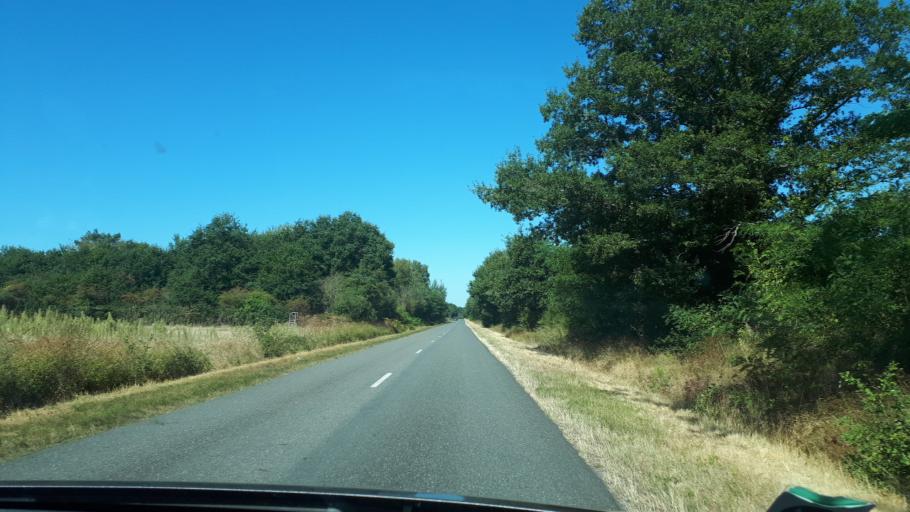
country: FR
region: Centre
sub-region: Departement du Loiret
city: Cerdon
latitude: 47.6385
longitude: 2.4133
